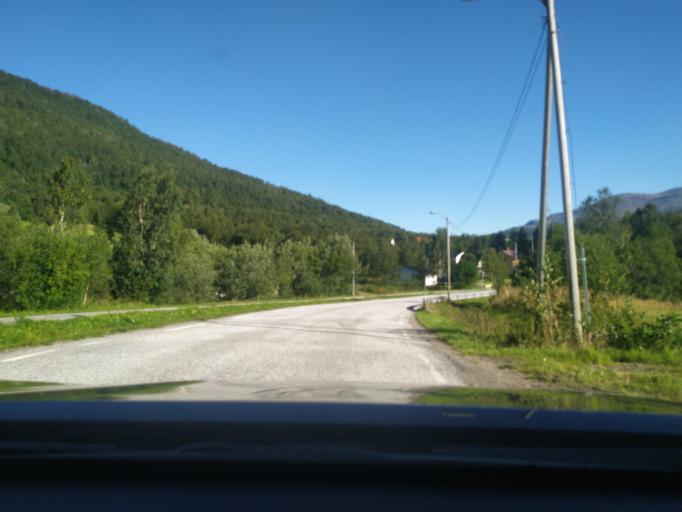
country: NO
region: Troms
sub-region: Salangen
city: Sjovegan
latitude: 68.9367
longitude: 17.7168
